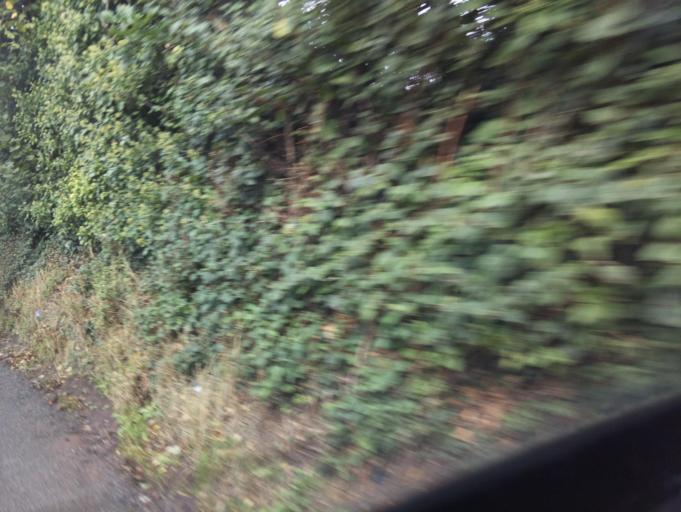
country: GB
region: England
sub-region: Worcestershire
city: Kidderminster
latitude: 52.3554
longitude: -2.1911
